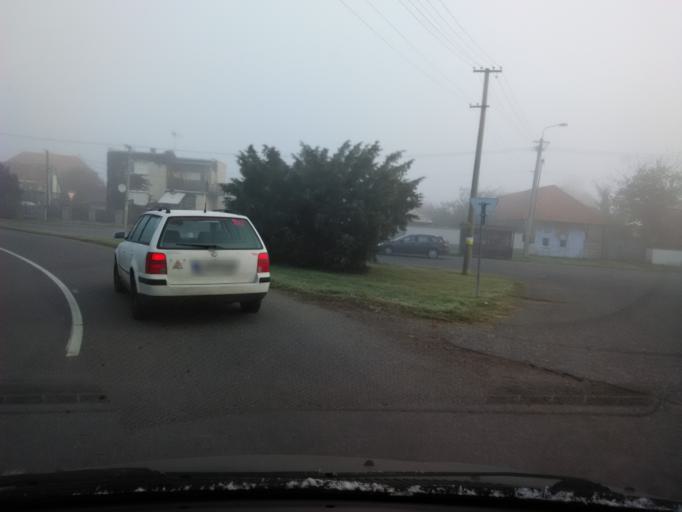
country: SK
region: Nitriansky
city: Levice
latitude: 48.2424
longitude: 18.5758
